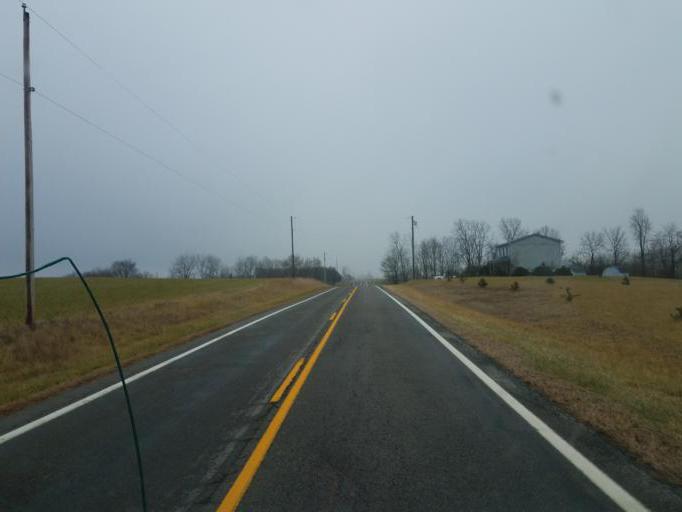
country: US
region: Ohio
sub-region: Champaign County
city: North Lewisburg
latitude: 40.2715
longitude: -83.5955
